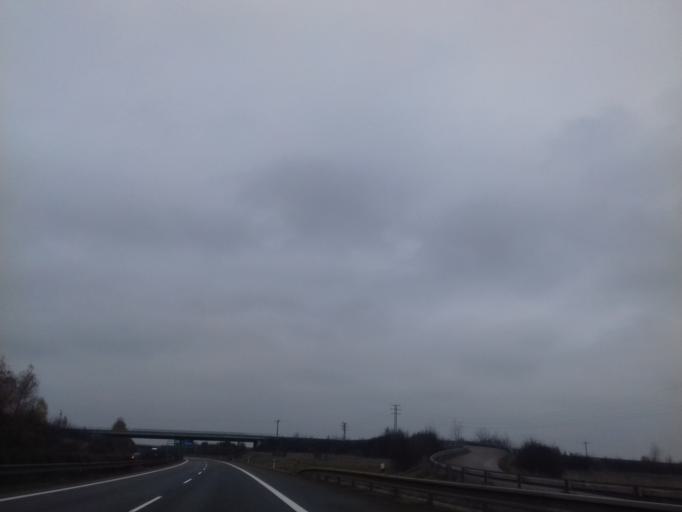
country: CZ
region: Plzensky
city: Stenovice
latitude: 49.6846
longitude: 13.3869
